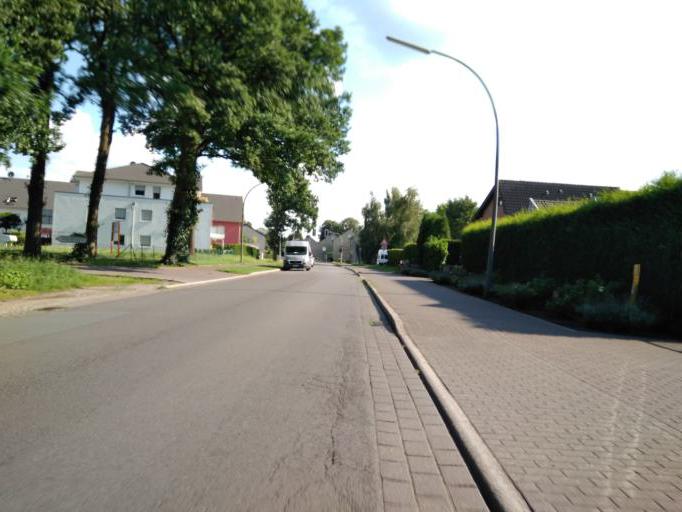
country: DE
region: North Rhine-Westphalia
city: Dorsten
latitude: 51.6877
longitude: 6.9593
